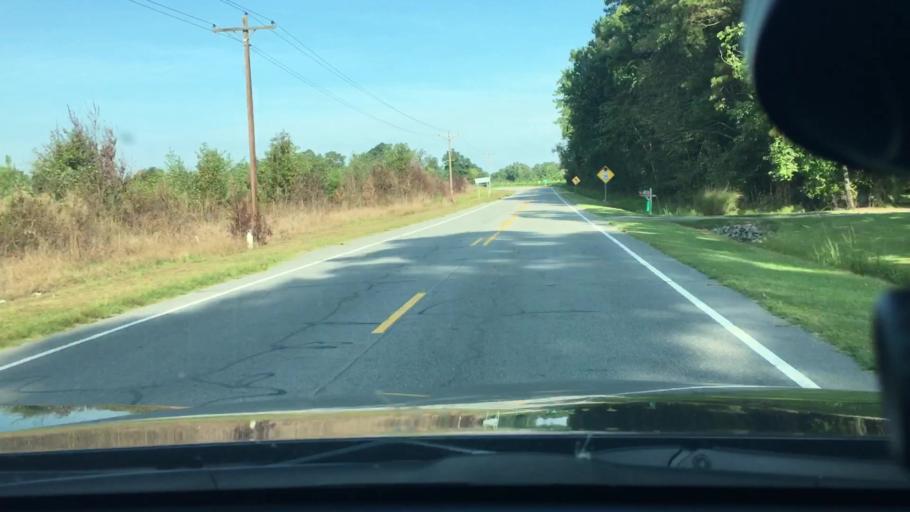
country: US
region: North Carolina
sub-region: Edgecombe County
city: Pinetops
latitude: 35.7873
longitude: -77.6232
